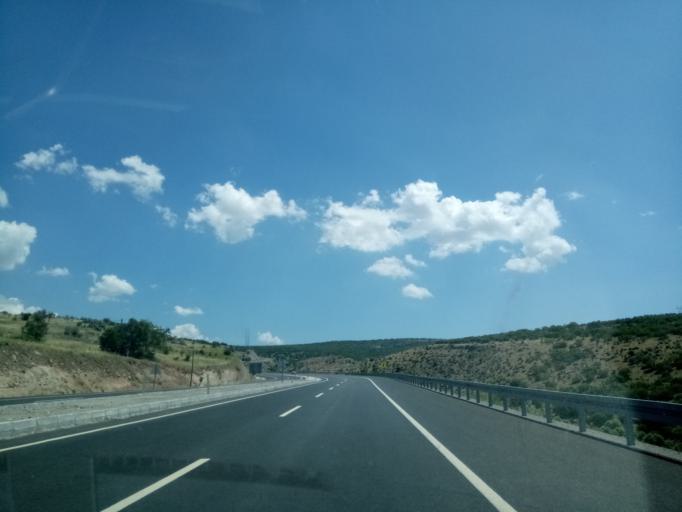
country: TR
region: Konya
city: Cavus
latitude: 37.6463
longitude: 31.9507
